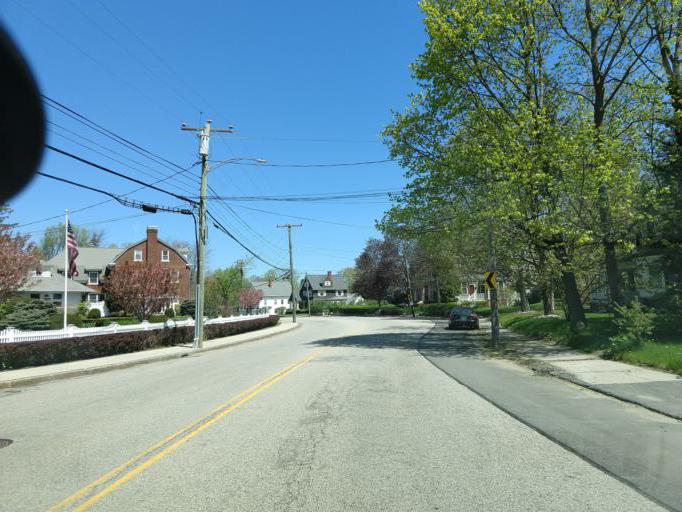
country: US
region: New Hampshire
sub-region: Rockingham County
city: Portsmouth
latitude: 43.0647
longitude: -70.7672
